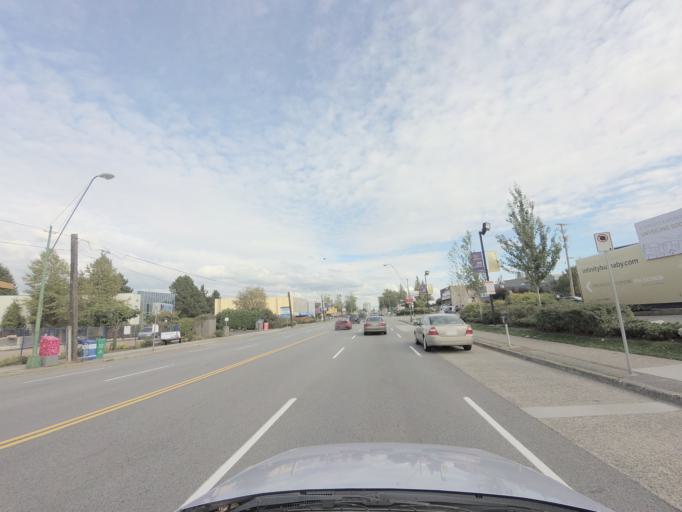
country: CA
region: British Columbia
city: Burnaby
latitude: 49.2236
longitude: -122.9847
